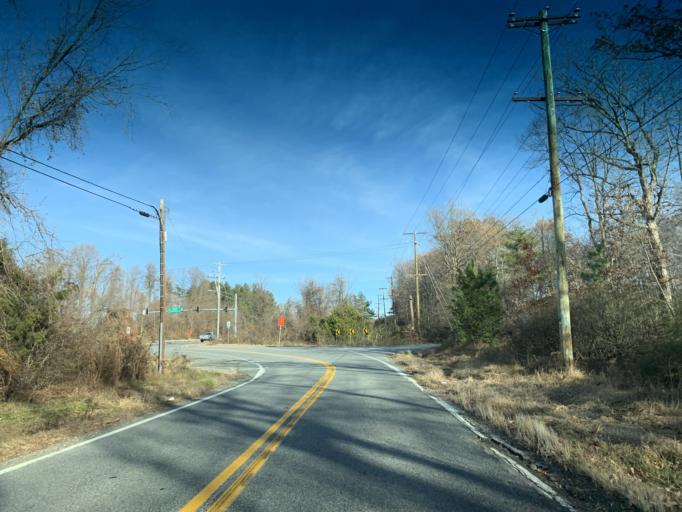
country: US
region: Maryland
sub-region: Cecil County
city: Charlestown
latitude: 39.5820
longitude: -76.0223
